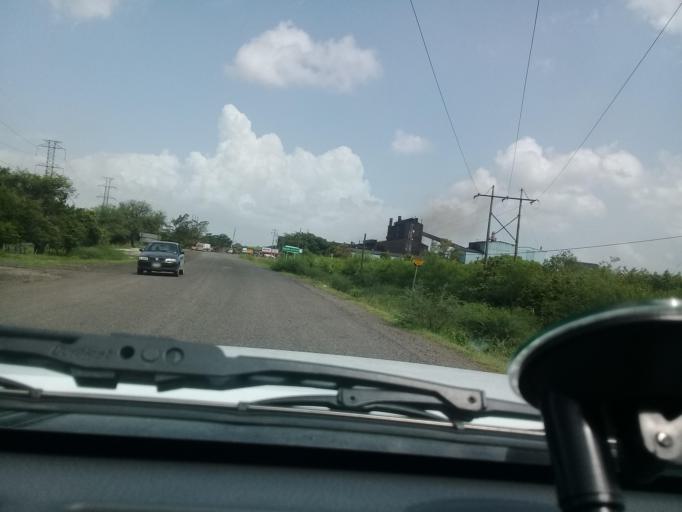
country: MX
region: Veracruz
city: Moralillo
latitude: 22.2317
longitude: -98.0195
